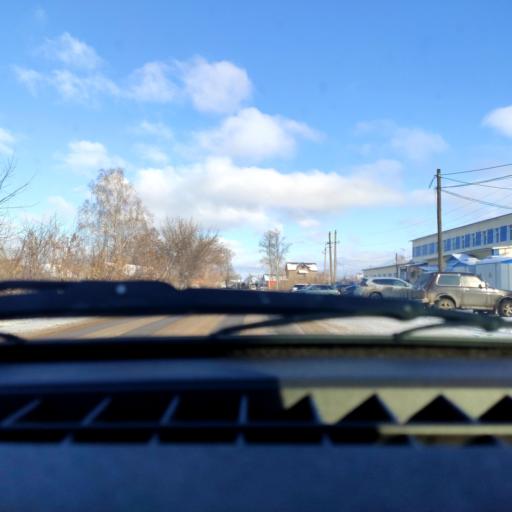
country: RU
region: Bashkortostan
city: Iglino
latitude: 54.8186
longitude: 56.3950
